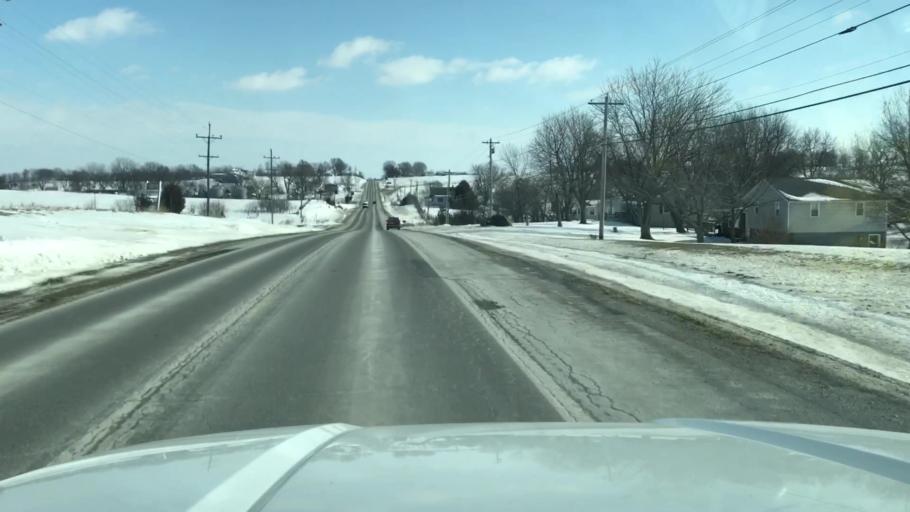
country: US
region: Missouri
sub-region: Nodaway County
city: Maryville
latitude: 40.3446
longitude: -94.8056
